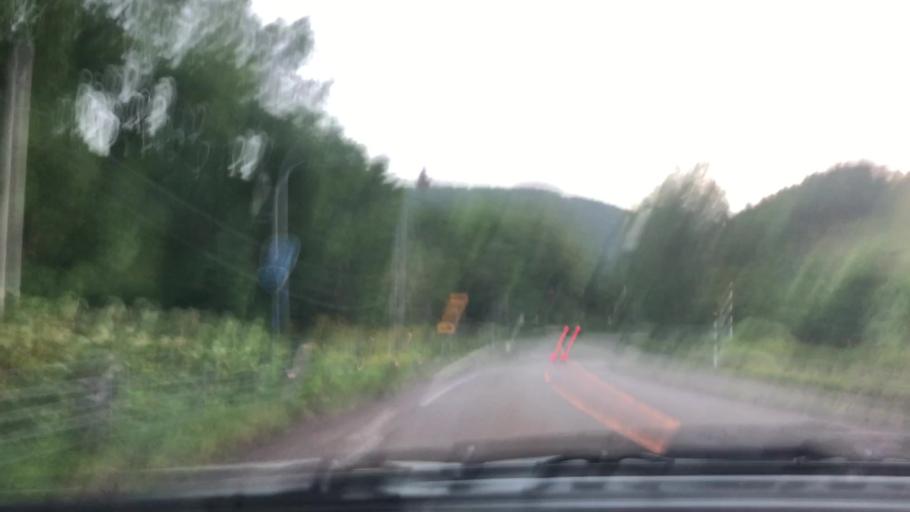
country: JP
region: Hokkaido
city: Iwamizawa
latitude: 42.9308
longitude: 142.0693
